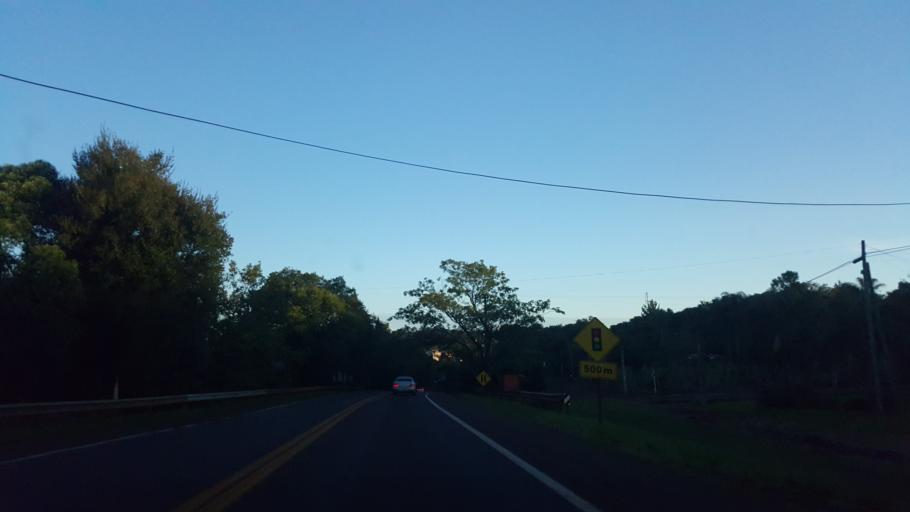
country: AR
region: Misiones
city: Capiovi
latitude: -26.9199
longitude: -55.0588
